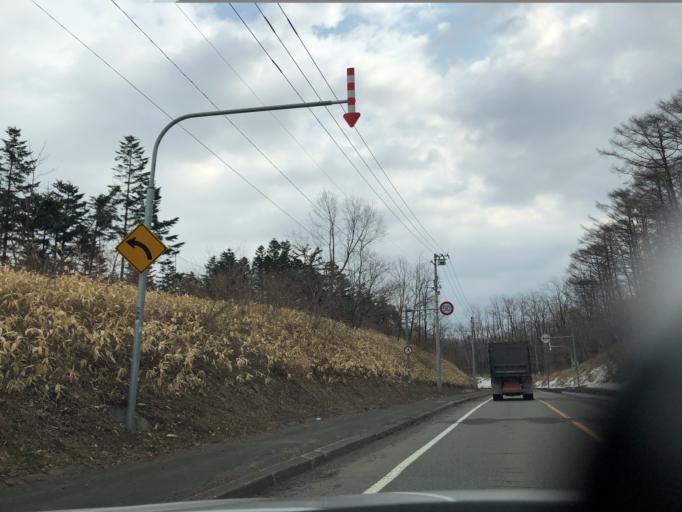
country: JP
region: Hokkaido
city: Chitose
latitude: 42.7584
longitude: 141.7922
